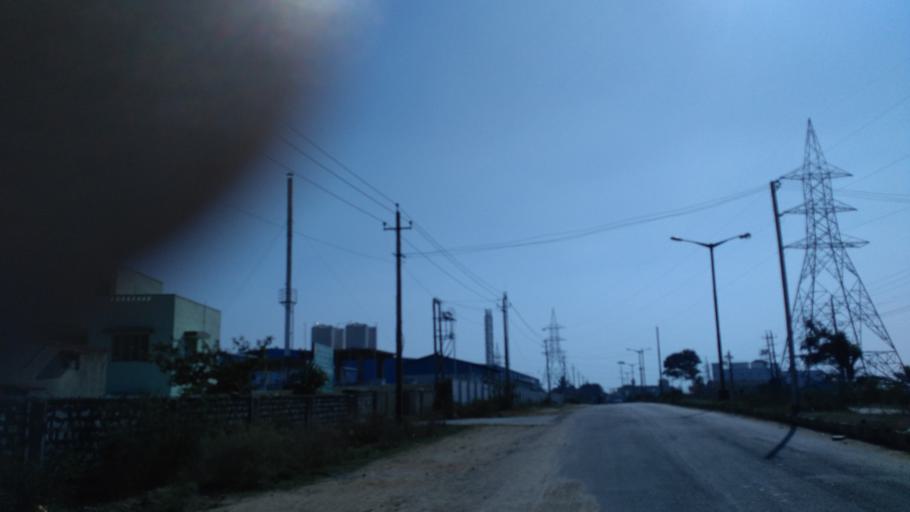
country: IN
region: Karnataka
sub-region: Hassan
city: Hassan
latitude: 12.9747
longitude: 76.1202
